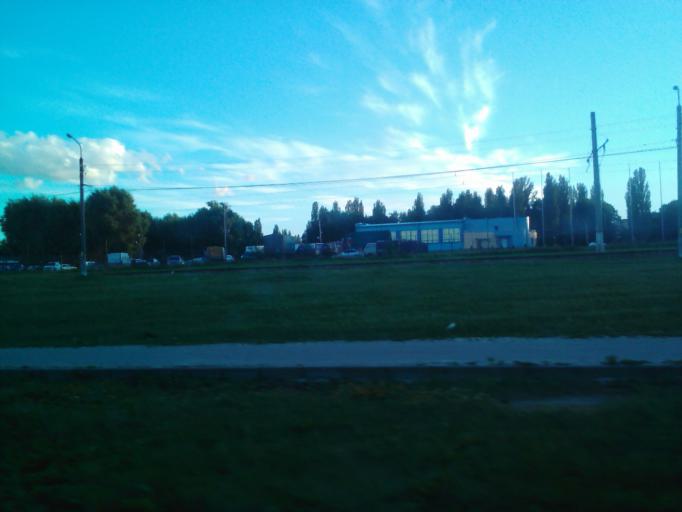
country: RU
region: Kursk
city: Kursk
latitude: 51.7372
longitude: 36.1514
